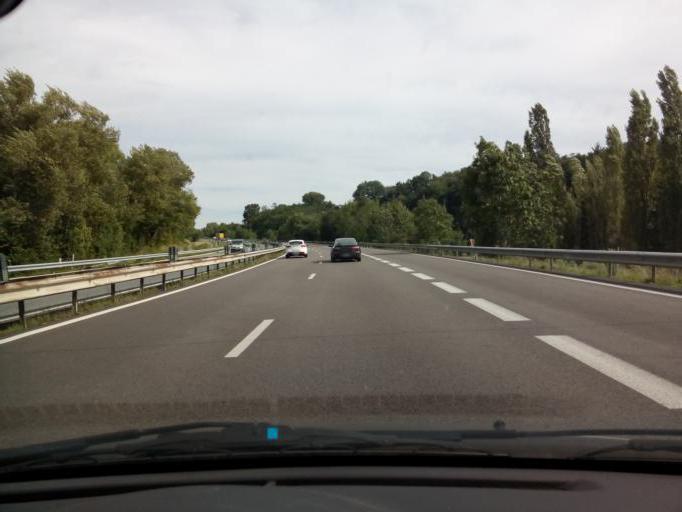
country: FR
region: Rhone-Alpes
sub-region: Departement de l'Isere
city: Cessieu
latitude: 45.5444
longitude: 5.3767
